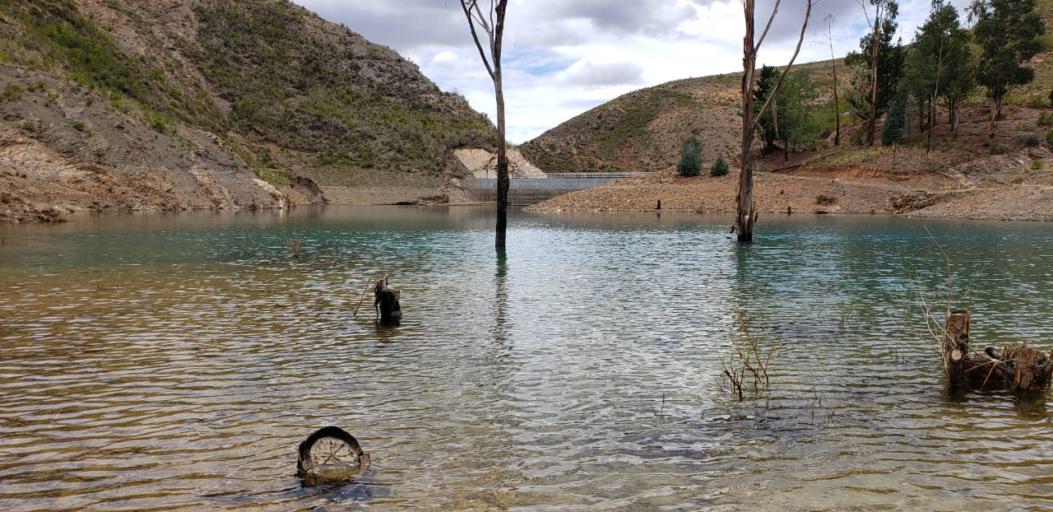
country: BO
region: Cochabamba
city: Tarata
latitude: -17.6593
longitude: -66.1316
